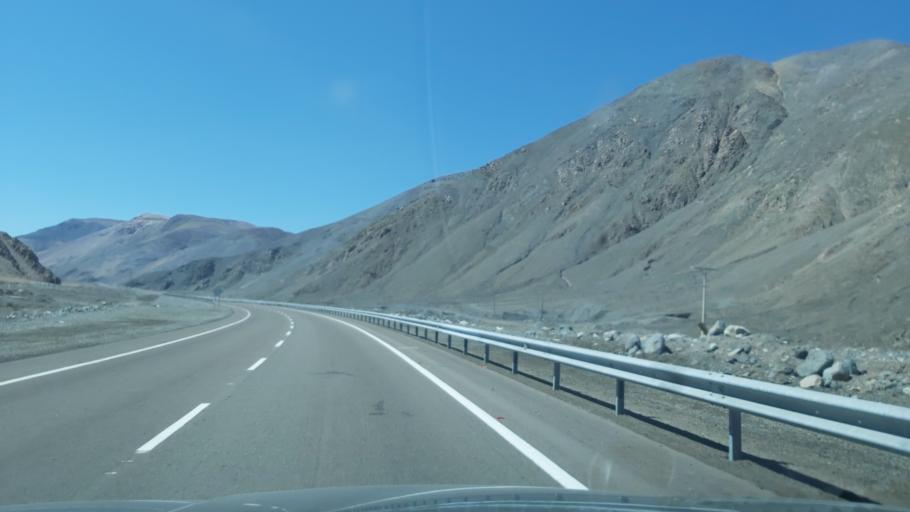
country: CL
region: Atacama
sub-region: Provincia de Chanaral
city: Diego de Almagro
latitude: -26.3491
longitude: -69.7407
